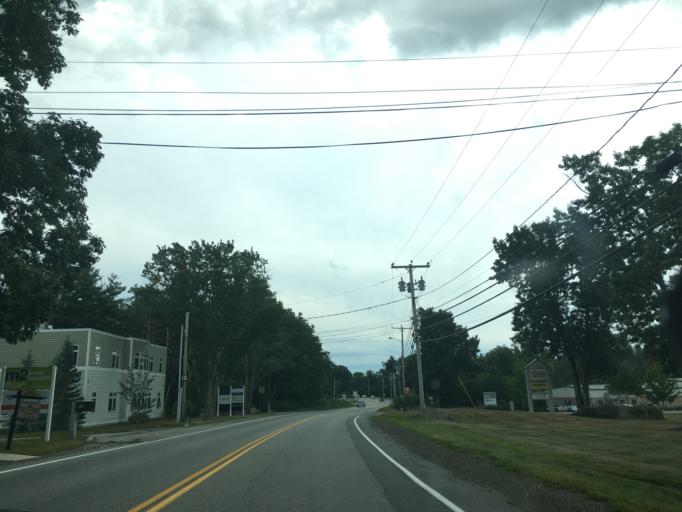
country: US
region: New Hampshire
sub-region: Rockingham County
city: Exeter
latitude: 42.9936
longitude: -70.9706
